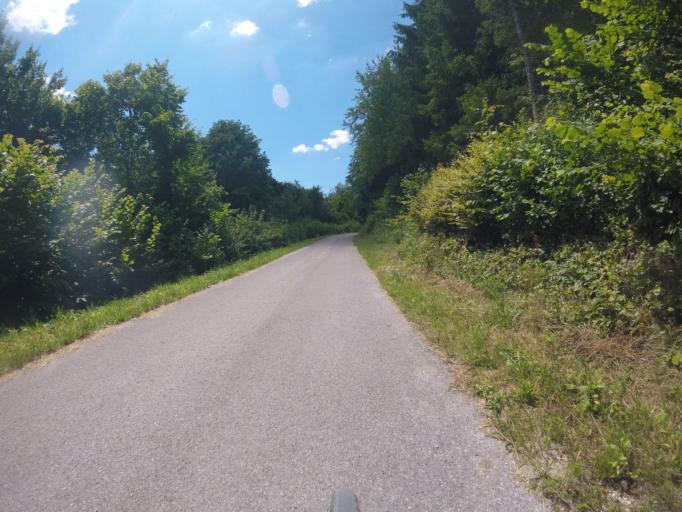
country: SI
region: Kostanjevica na Krki
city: Kostanjevica na Krki
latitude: 45.7564
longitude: 15.3927
